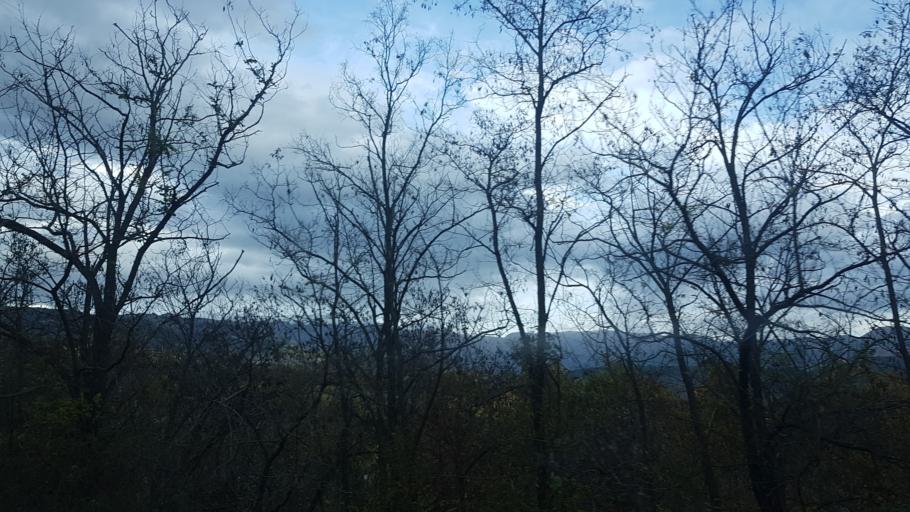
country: IT
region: Abruzzo
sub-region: Provincia dell' Aquila
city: L'Aquila
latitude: 42.3645
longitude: 13.4281
